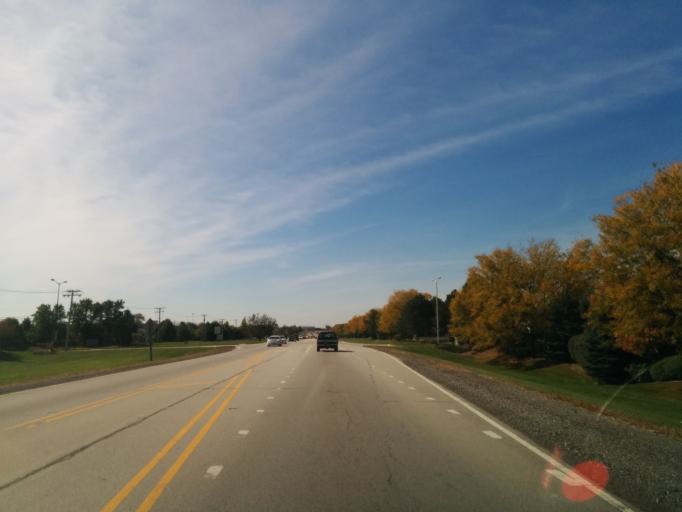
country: US
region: Illinois
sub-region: Kane County
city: Batavia
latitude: 41.8149
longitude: -88.2672
